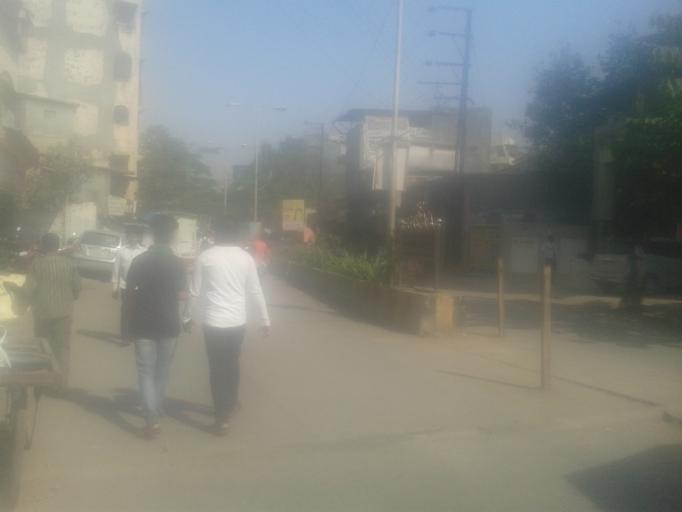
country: IN
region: Maharashtra
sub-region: Thane
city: Ulhasnagar
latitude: 19.2201
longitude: 73.1618
